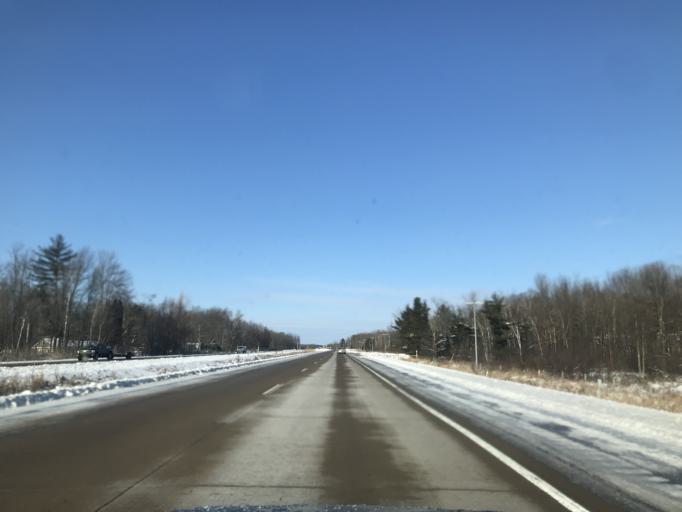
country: US
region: Wisconsin
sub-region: Oconto County
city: Oconto Falls
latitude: 44.8079
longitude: -88.0489
